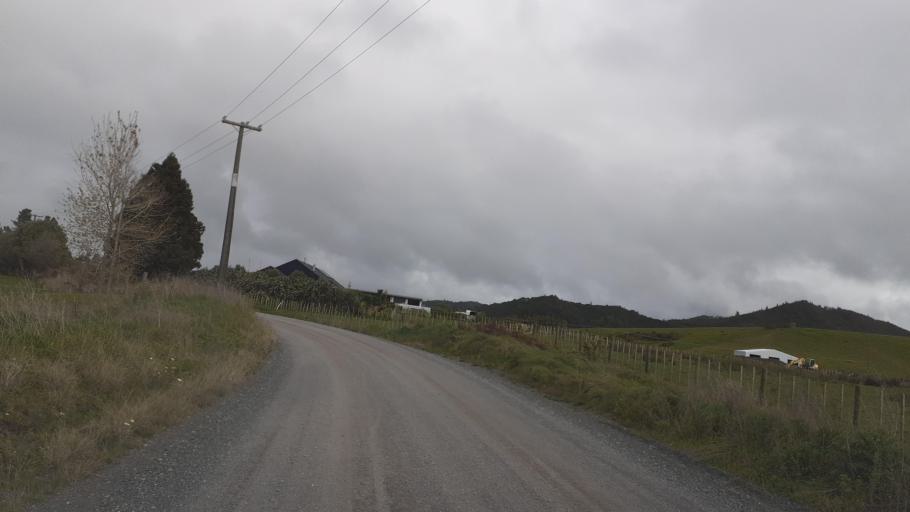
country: NZ
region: Northland
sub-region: Far North District
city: Waimate North
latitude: -35.2438
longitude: 173.7989
